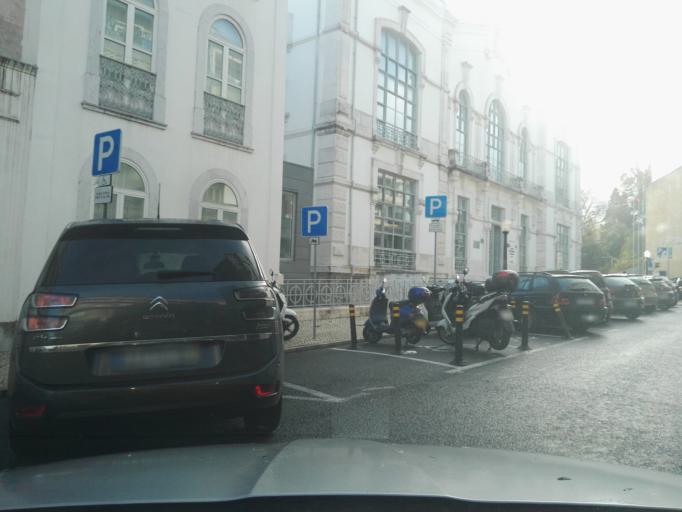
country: PT
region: Lisbon
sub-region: Lisbon
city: Lisbon
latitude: 38.7176
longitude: -9.1595
